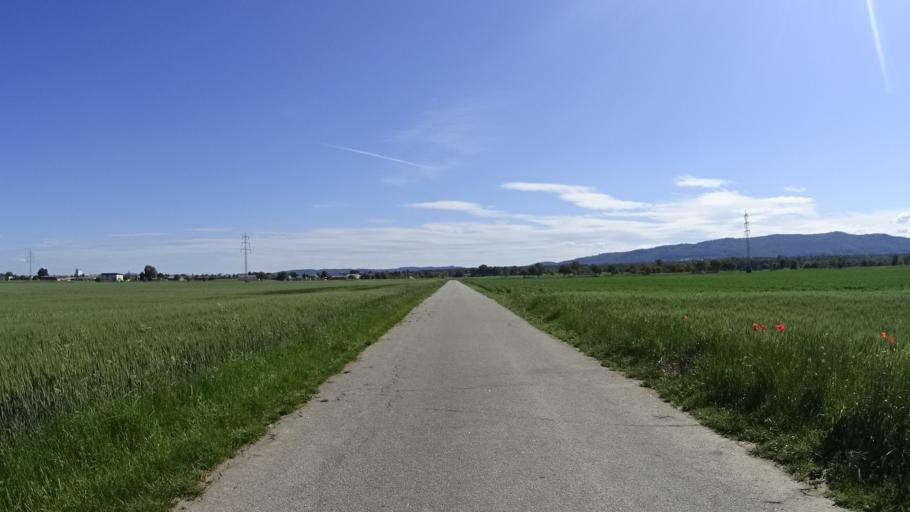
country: DE
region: Hesse
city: Pfungstadt
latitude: 49.7806
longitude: 8.5896
